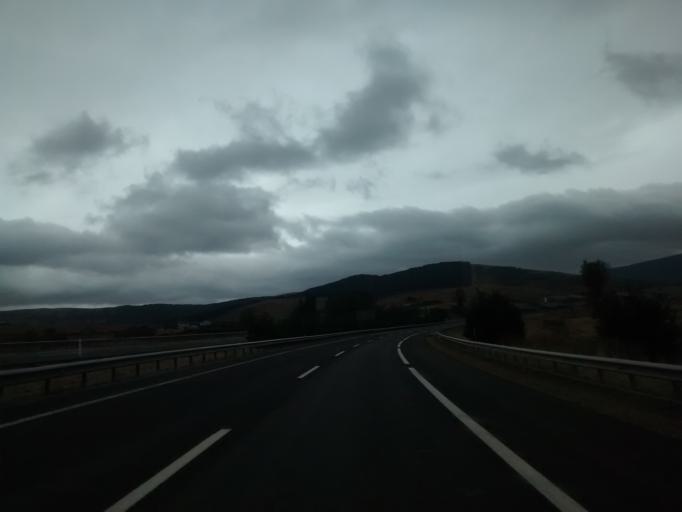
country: ES
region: Cantabria
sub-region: Provincia de Cantabria
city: Reinosa
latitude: 42.9966
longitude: -4.1251
